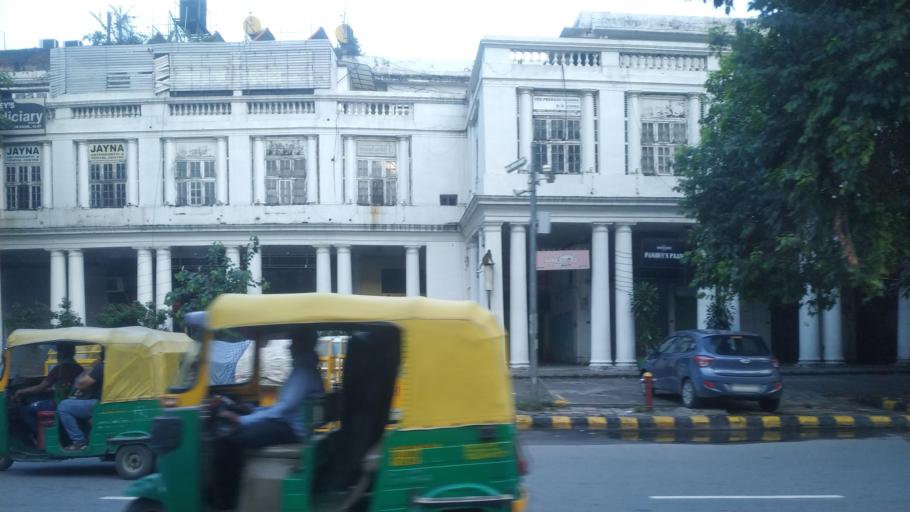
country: IN
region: NCT
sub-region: New Delhi
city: New Delhi
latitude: 28.6322
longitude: 77.2227
